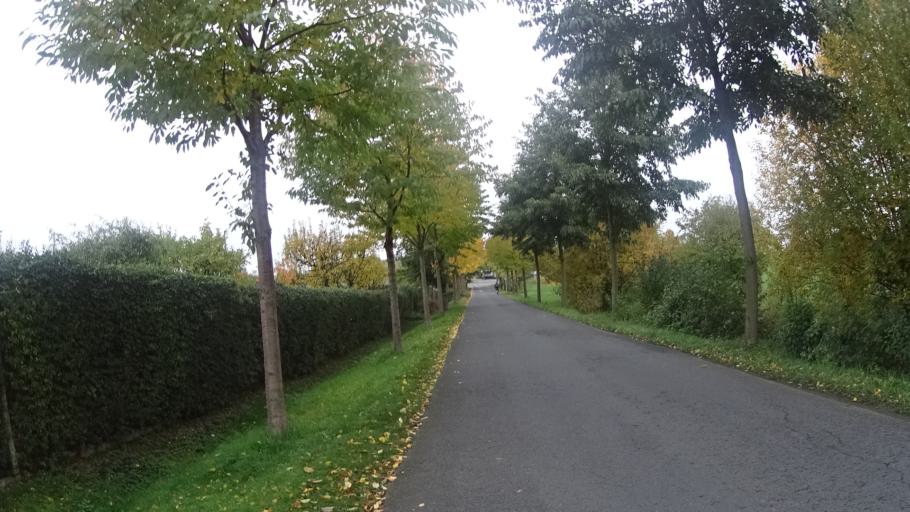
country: DE
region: Thuringia
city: Arnstadt
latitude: 50.8454
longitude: 10.9311
